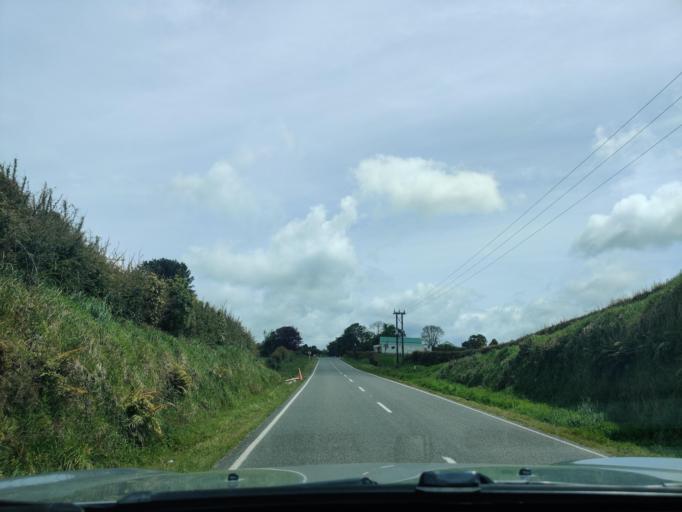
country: NZ
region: Taranaki
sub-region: South Taranaki District
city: Eltham
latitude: -39.3767
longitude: 174.1759
